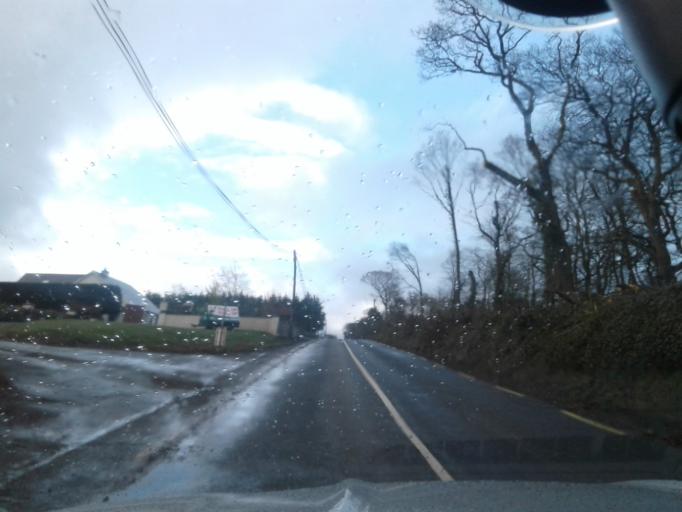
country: IE
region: Ulster
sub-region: County Donegal
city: Ramelton
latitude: 55.0238
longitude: -7.6510
